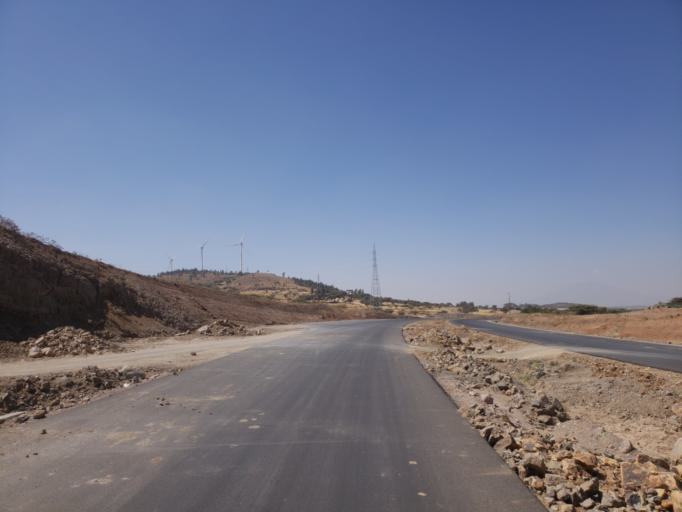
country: ET
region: Oromiya
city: Mojo
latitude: 8.5657
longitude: 39.1622
